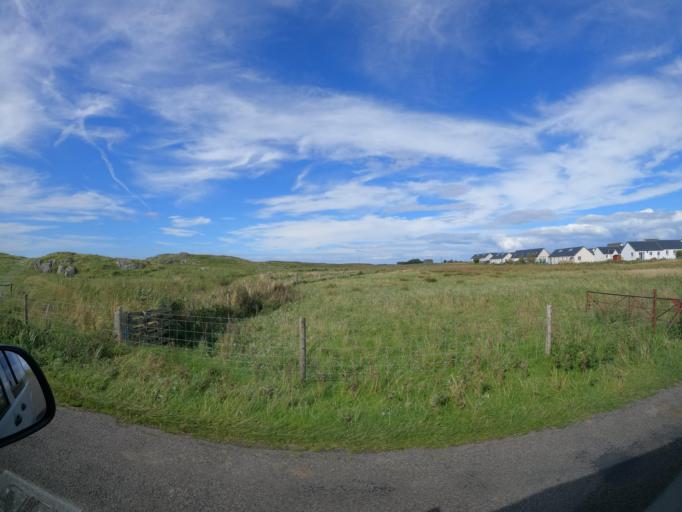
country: GB
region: Scotland
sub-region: Eilean Siar
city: Barra
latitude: 56.5047
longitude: -6.8030
